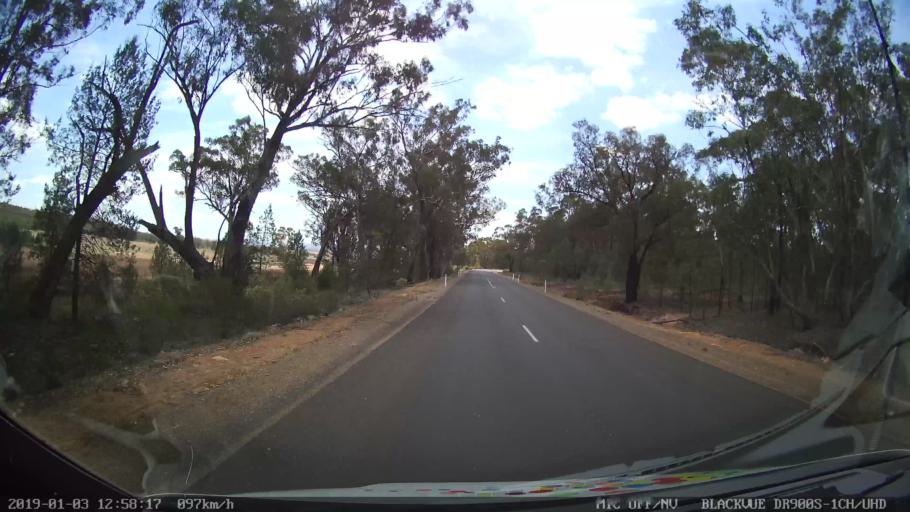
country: AU
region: New South Wales
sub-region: Cabonne
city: Canowindra
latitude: -33.6433
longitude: 148.3732
